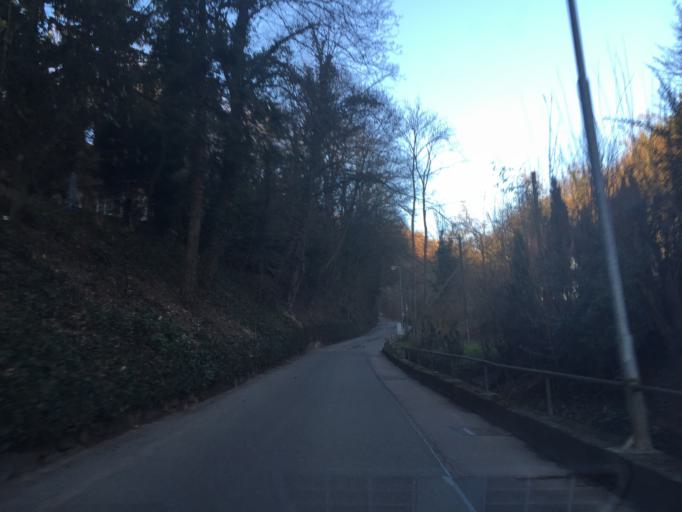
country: DE
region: Baden-Wuerttemberg
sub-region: Karlsruhe Region
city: Weinheim
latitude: 49.5208
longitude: 8.6761
